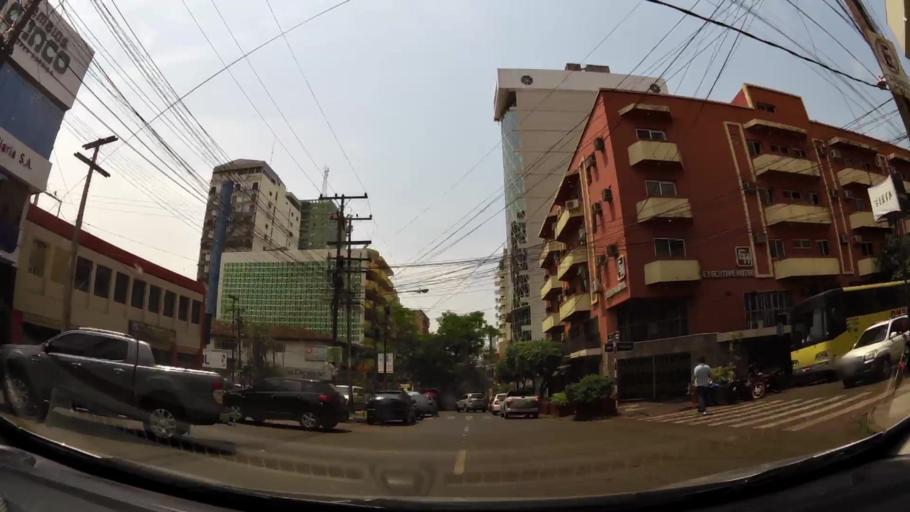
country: PY
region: Alto Parana
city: Ciudad del Este
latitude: -25.5107
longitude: -54.6131
